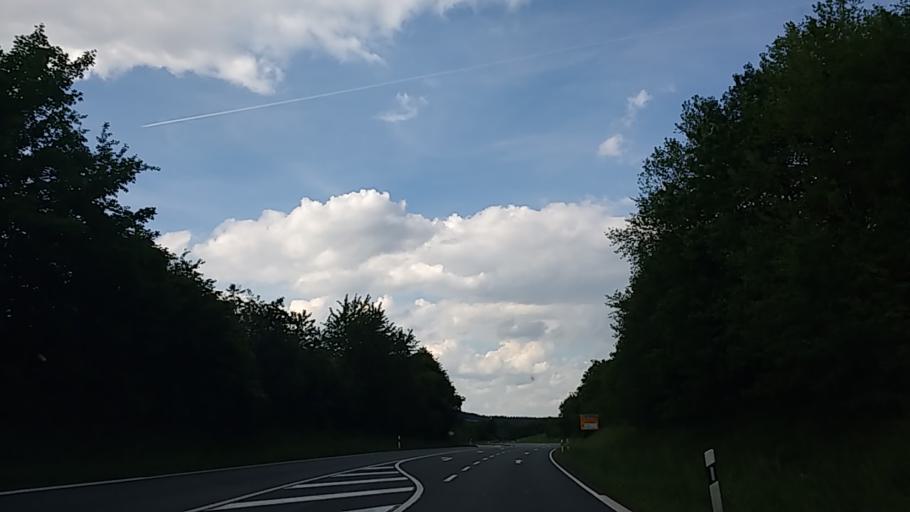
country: DE
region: Hesse
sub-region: Regierungsbezirk Kassel
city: Bad Arolsen
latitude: 51.3711
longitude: 8.9964
